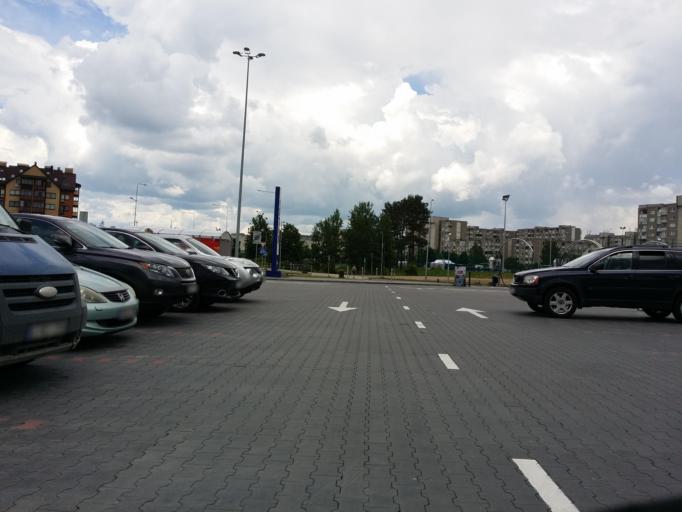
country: LT
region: Vilnius County
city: Pilaite
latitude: 54.7010
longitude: 25.1790
